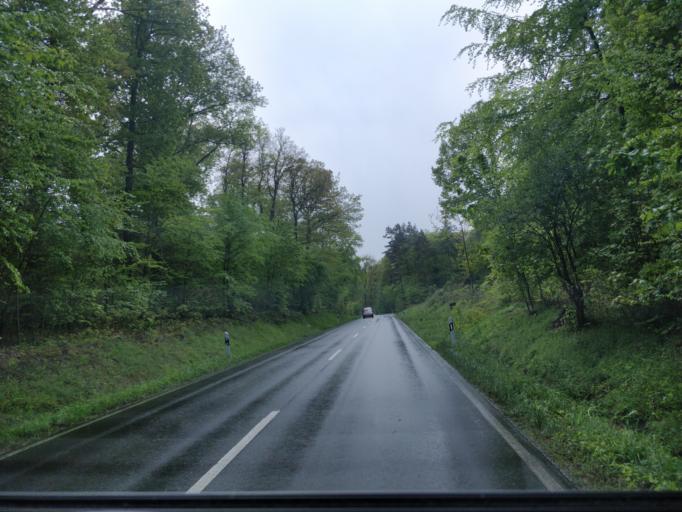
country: DE
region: North Rhine-Westphalia
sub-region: Regierungsbezirk Koln
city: Rheinbach
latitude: 50.6097
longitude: 6.9073
